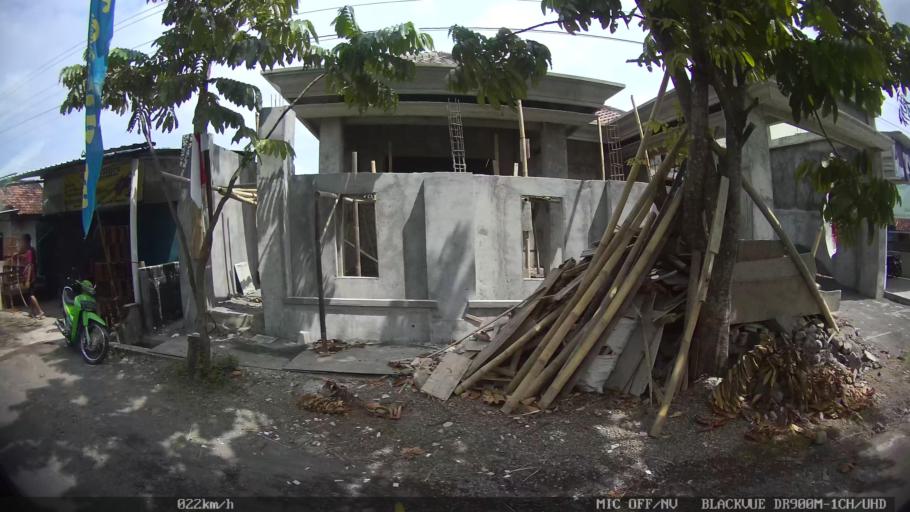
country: ID
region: Daerah Istimewa Yogyakarta
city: Depok
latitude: -7.7994
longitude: 110.4554
